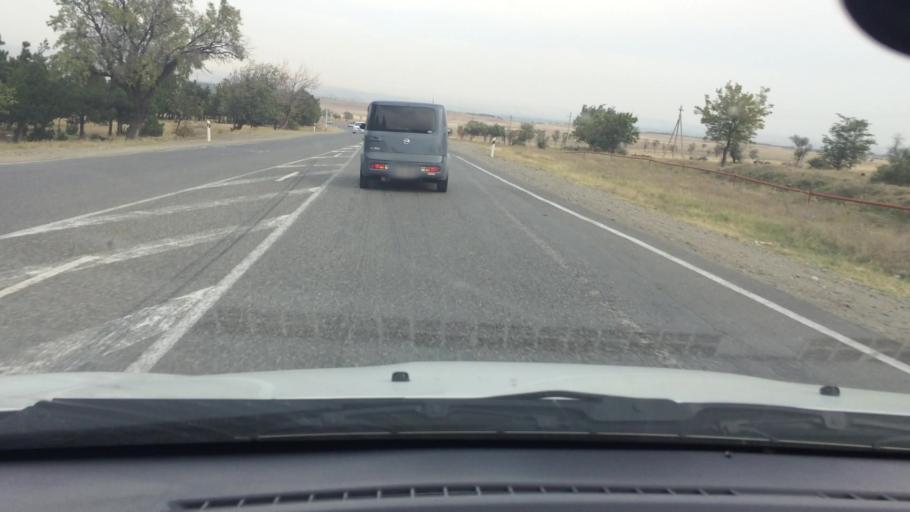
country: GE
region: T'bilisi
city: Tbilisi
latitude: 41.6390
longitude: 44.8703
